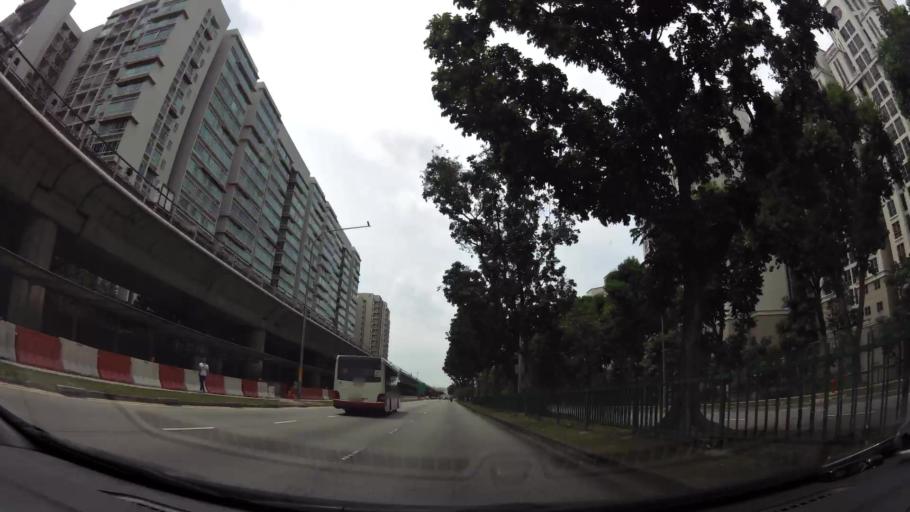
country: MY
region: Johor
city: Johor Bahru
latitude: 1.3437
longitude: 103.7185
